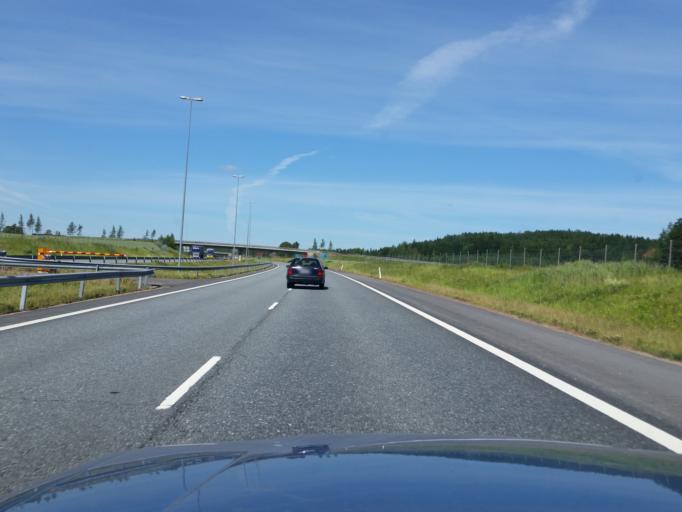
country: FI
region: Varsinais-Suomi
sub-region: Salo
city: Muurla
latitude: 60.3839
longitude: 23.3102
